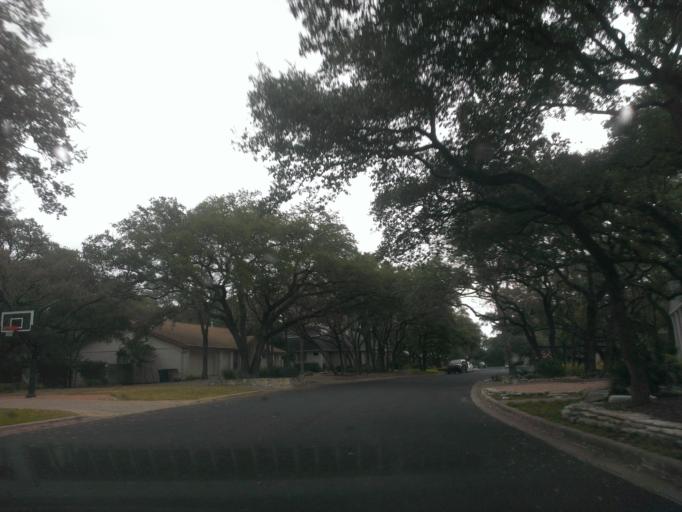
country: US
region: Texas
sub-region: Travis County
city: West Lake Hills
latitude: 30.3666
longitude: -97.7702
